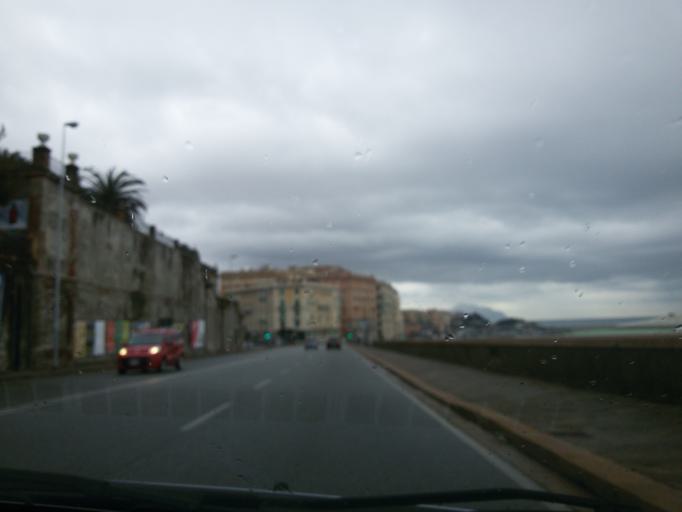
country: IT
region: Liguria
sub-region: Provincia di Genova
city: San Teodoro
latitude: 44.3979
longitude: 8.9373
